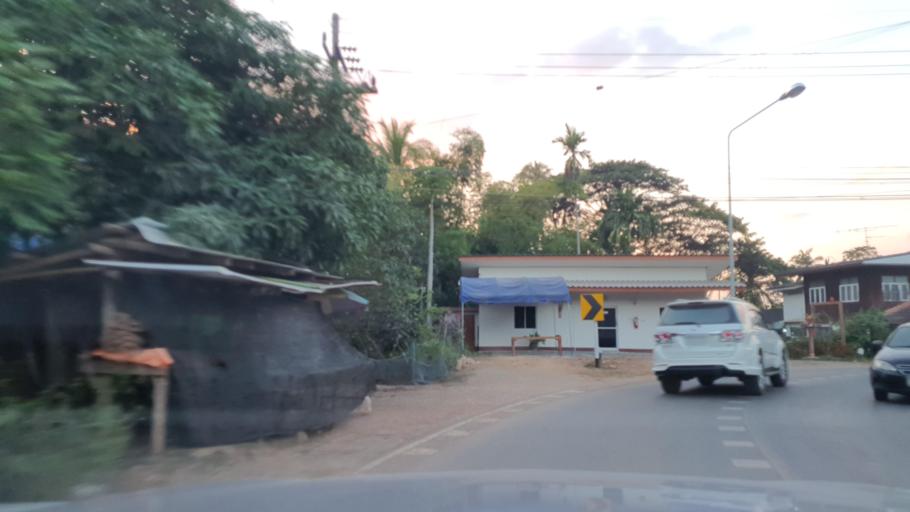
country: TH
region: Phayao
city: Dok Kham Tai
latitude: 19.0391
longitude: 100.0631
